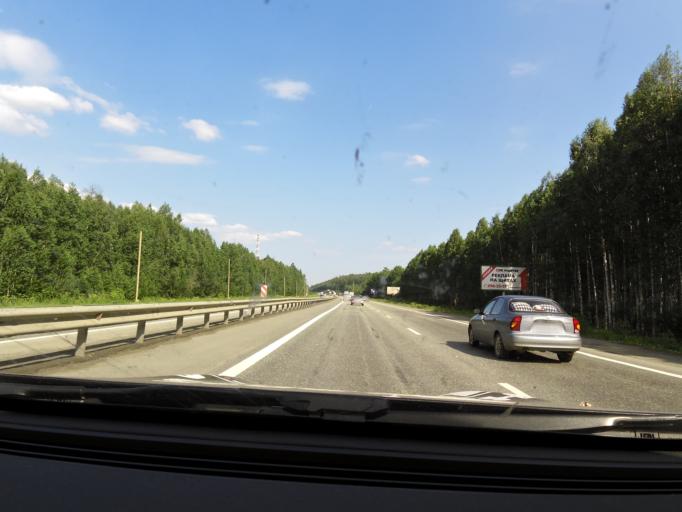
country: RU
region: Sverdlovsk
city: Severka
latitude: 56.8368
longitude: 60.2807
